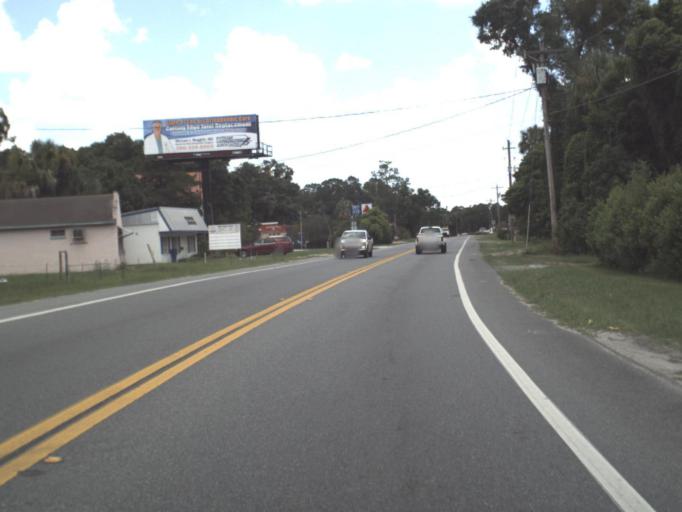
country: US
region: Florida
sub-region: Putnam County
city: Palatka
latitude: 29.5540
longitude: -81.6560
